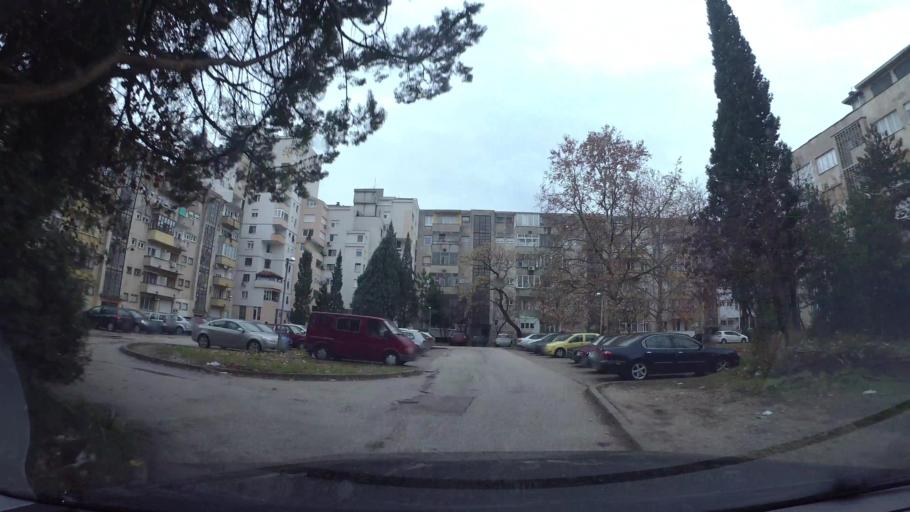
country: BA
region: Federation of Bosnia and Herzegovina
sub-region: Hercegovacko-Bosanski Kanton
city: Mostar
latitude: 43.3449
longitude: 17.7985
